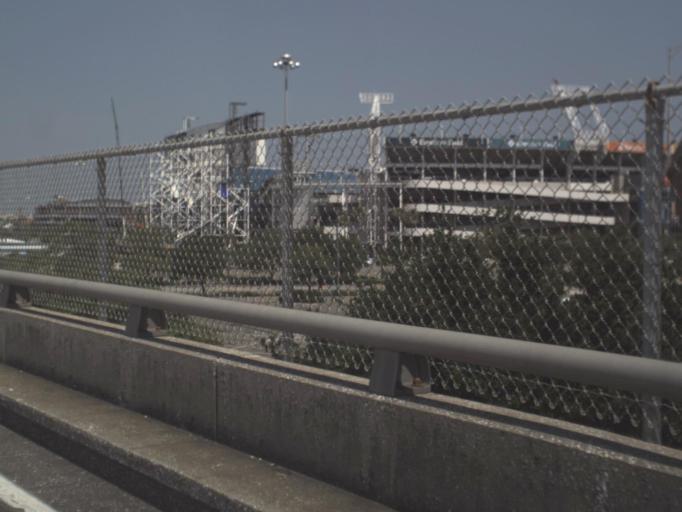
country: US
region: Florida
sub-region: Duval County
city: Jacksonville
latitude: 30.3208
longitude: -81.6342
